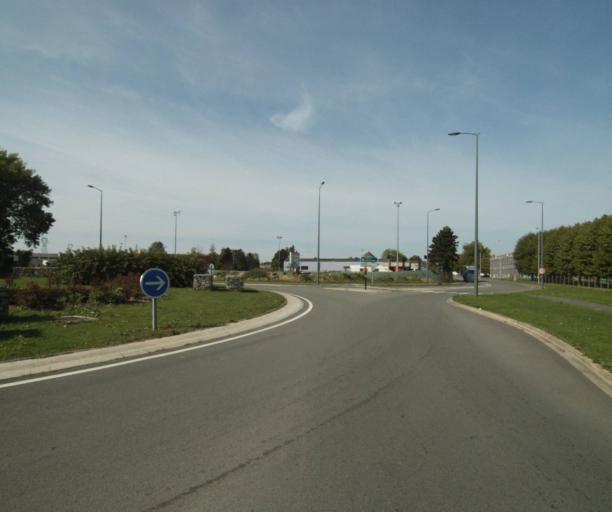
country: FR
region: Nord-Pas-de-Calais
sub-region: Departement du Nord
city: Sequedin
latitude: 50.6343
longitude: 2.9731
